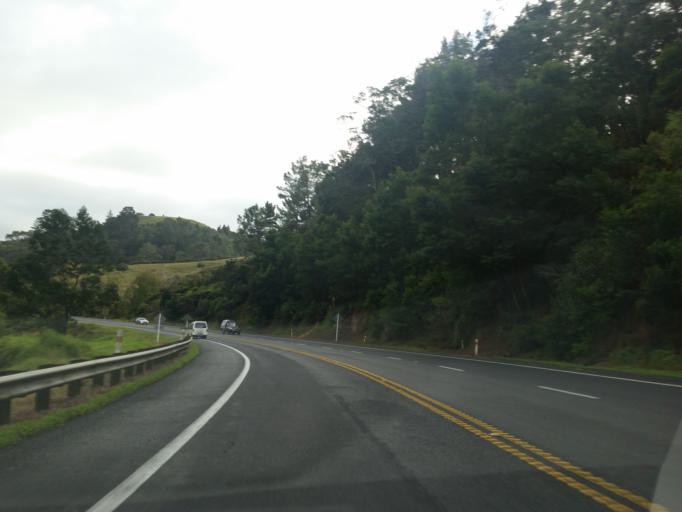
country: NZ
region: Waikato
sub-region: Hauraki District
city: Paeroa
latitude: -37.4046
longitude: 175.7082
